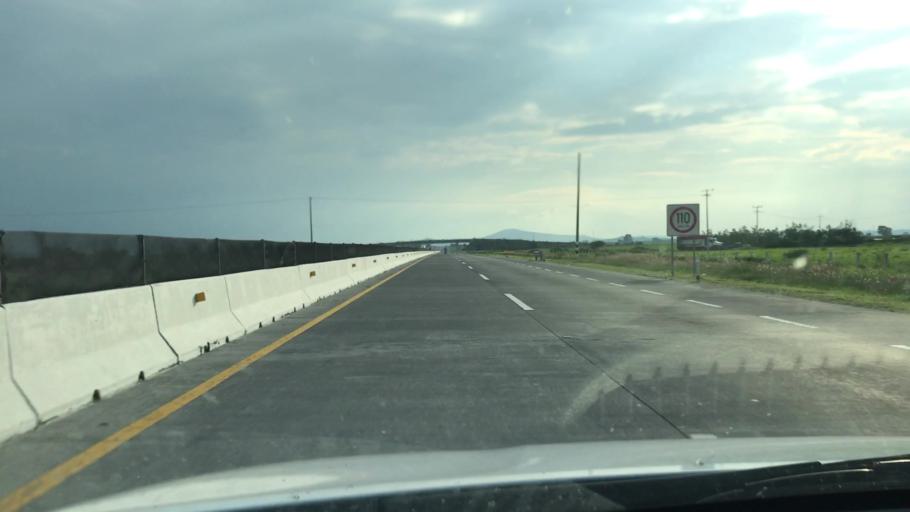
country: MX
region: Guanajuato
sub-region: Penjamo
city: Estacion la Piedad
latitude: 20.4030
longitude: -102.0332
